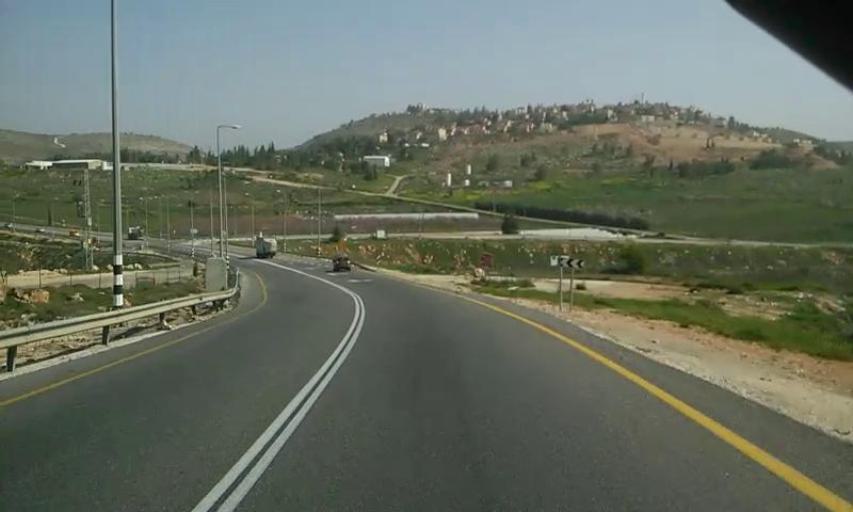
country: PS
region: West Bank
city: Turmus`ayya
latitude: 32.0515
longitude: 35.2887
